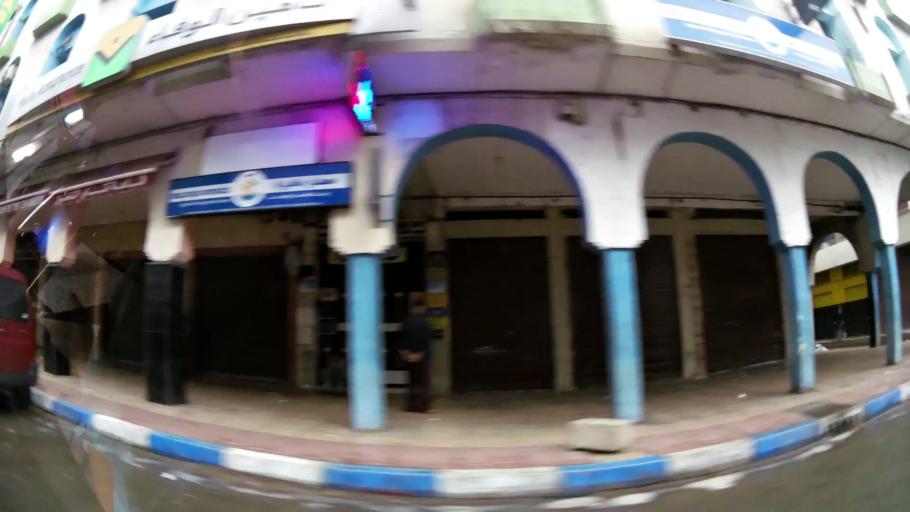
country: MA
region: Oriental
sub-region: Nador
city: Nador
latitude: 35.1767
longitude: -2.9289
